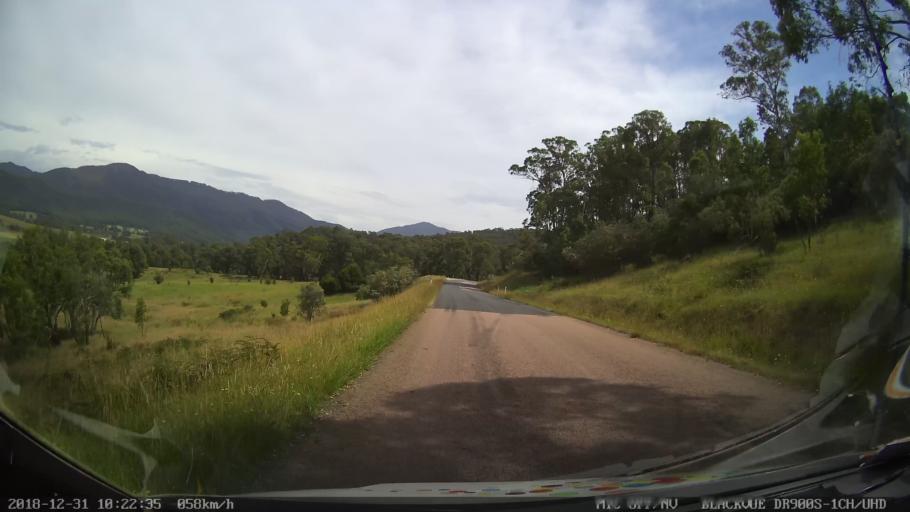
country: AU
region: New South Wales
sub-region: Snowy River
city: Jindabyne
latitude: -36.5243
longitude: 148.1432
